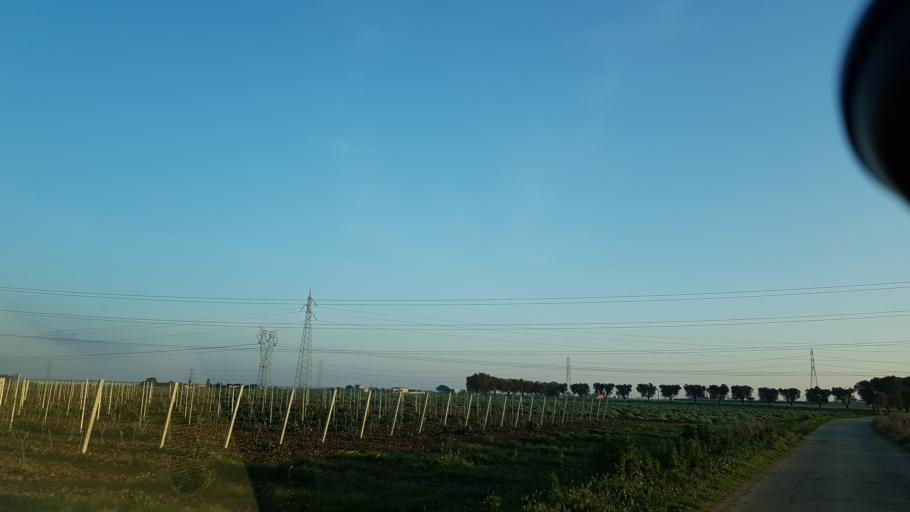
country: IT
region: Apulia
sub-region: Provincia di Brindisi
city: La Rosa
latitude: 40.6018
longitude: 17.9397
